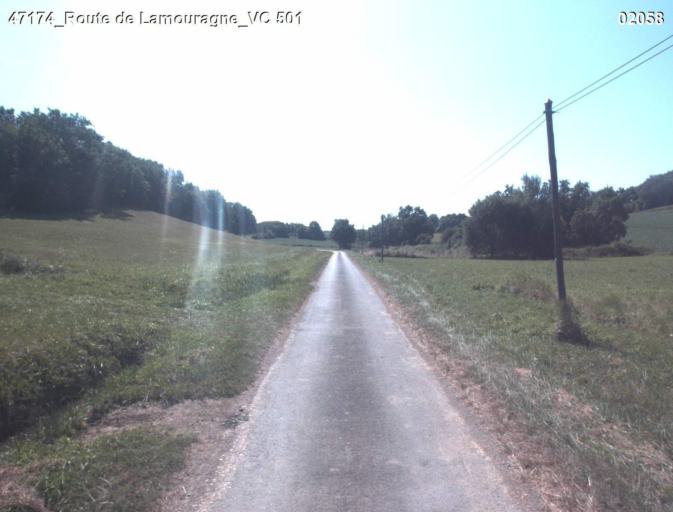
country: FR
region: Midi-Pyrenees
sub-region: Departement du Gers
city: Condom
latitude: 44.0308
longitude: 0.3941
